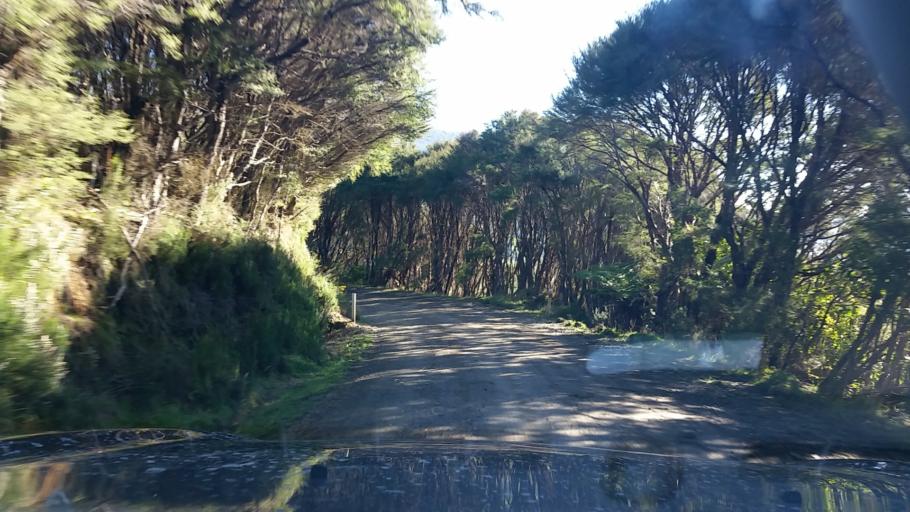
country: NZ
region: Marlborough
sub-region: Marlborough District
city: Picton
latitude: -41.1352
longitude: 174.0539
